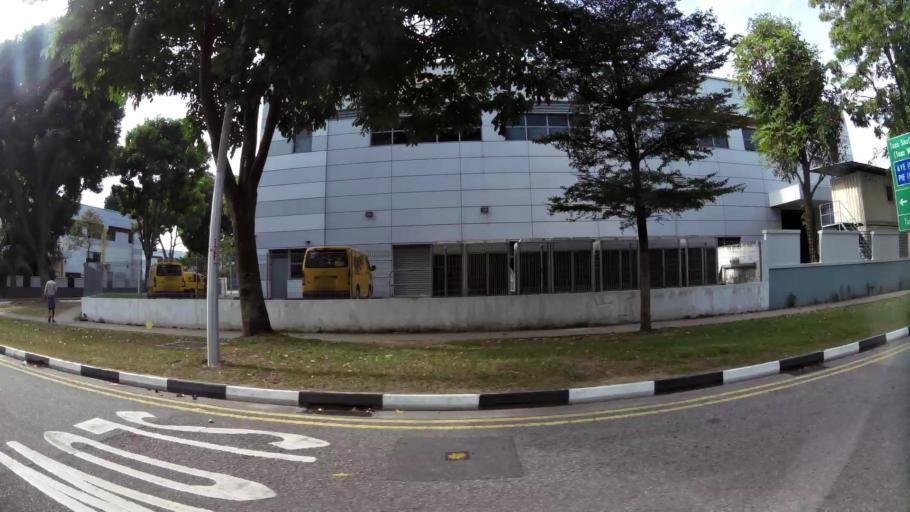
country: MY
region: Johor
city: Johor Bahru
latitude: 1.3122
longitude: 103.6291
